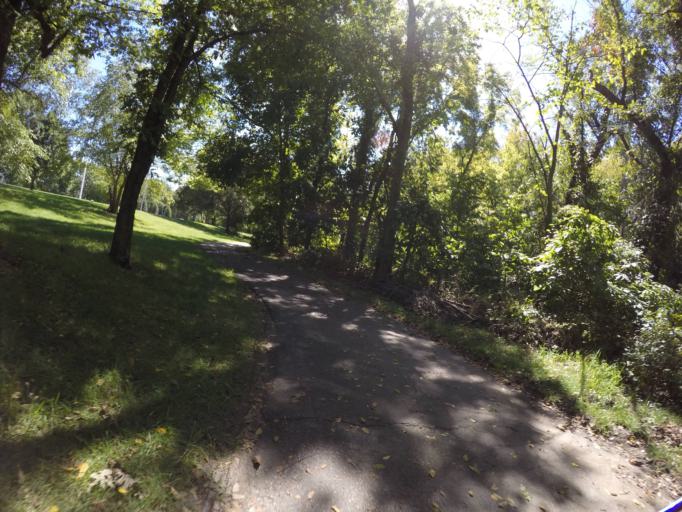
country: US
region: Kansas
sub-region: Johnson County
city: Lenexa
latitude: 38.9305
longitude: -94.6971
